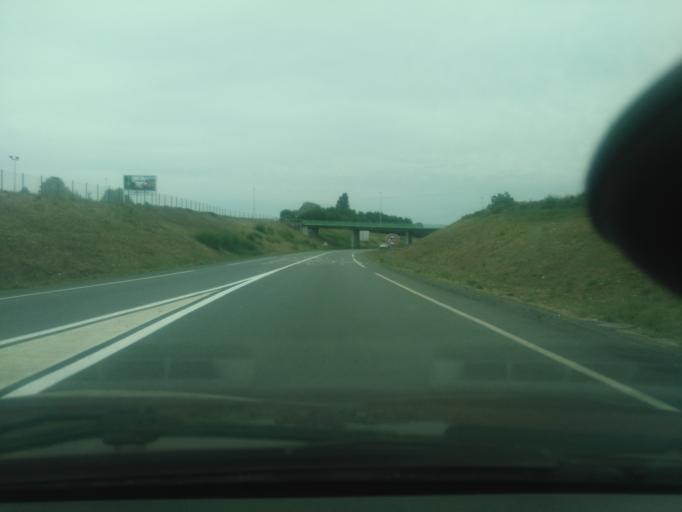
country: FR
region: Pays de la Loire
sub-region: Departement de la Vendee
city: Chantonnay
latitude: 46.6980
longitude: -1.0429
